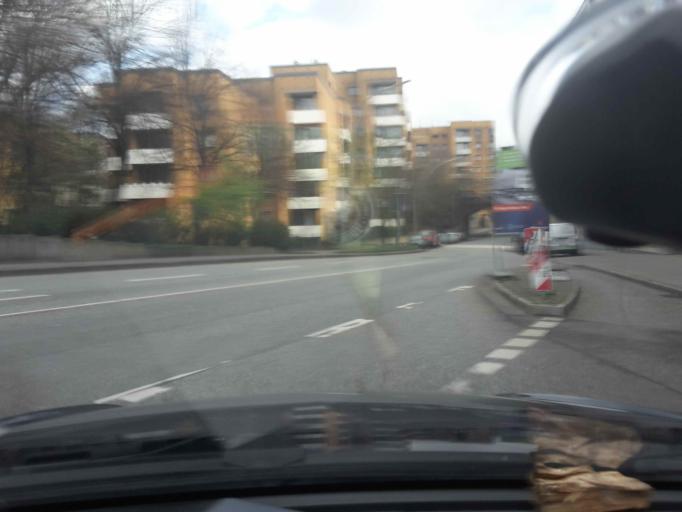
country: DE
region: Hamburg
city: St. Pauli
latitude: 53.5464
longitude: 9.9534
